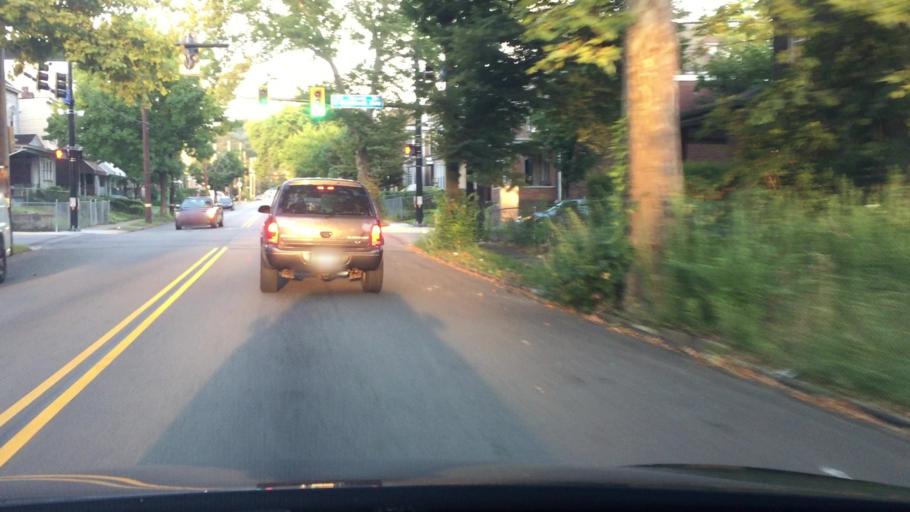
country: US
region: Pennsylvania
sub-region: Allegheny County
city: Wilkinsburg
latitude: 40.4551
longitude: -79.8908
